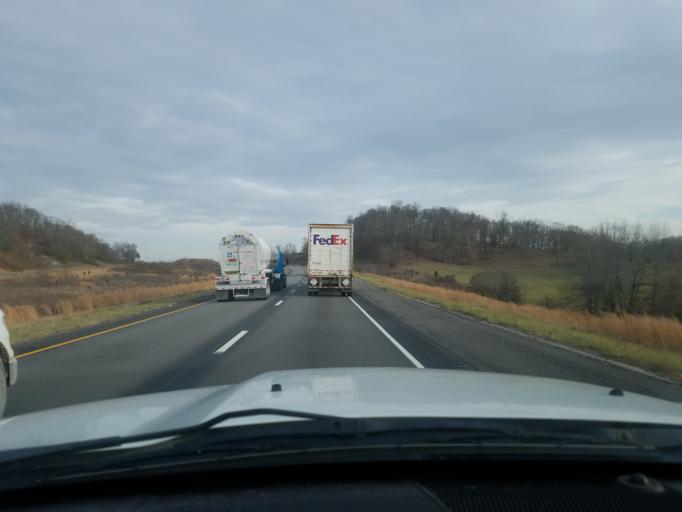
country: US
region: Indiana
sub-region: Dubois County
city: Ferdinand
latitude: 38.2031
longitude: -86.8404
